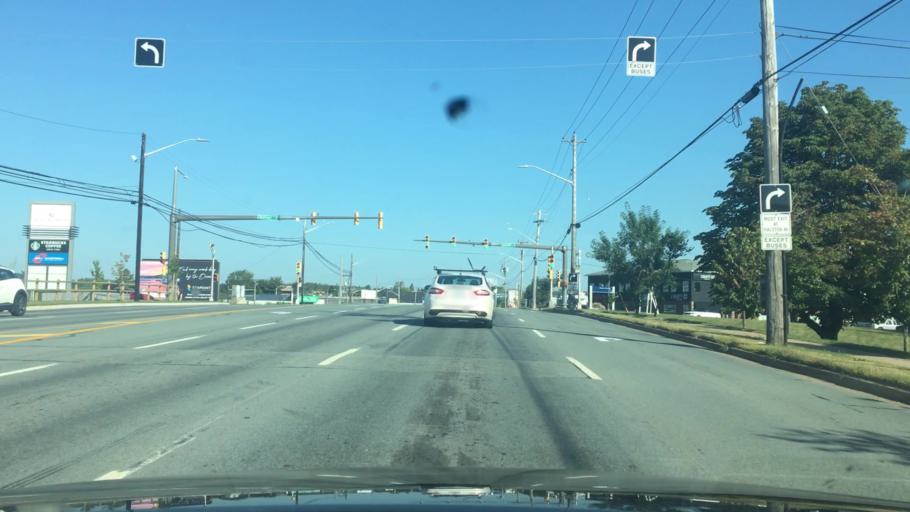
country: CA
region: Nova Scotia
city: Dartmouth
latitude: 44.7001
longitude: -63.6065
